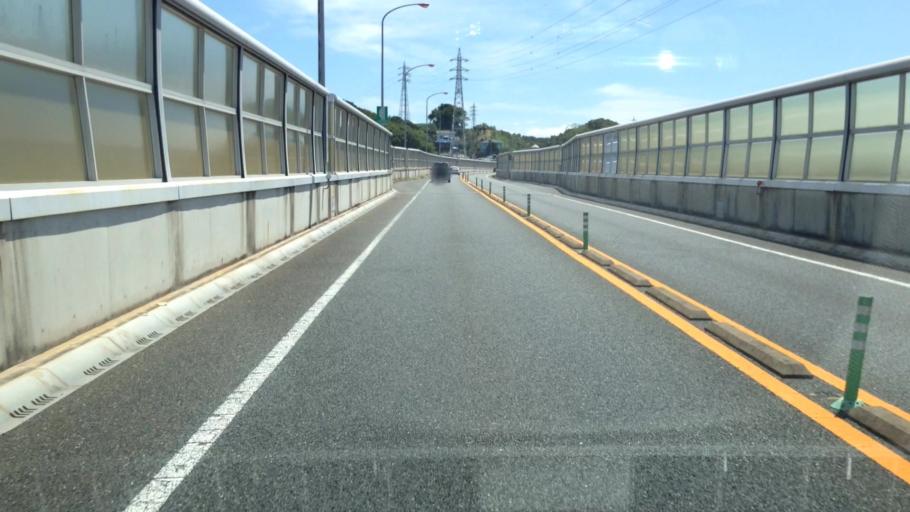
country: JP
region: Kanagawa
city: Yokosuka
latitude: 35.2193
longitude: 139.6372
